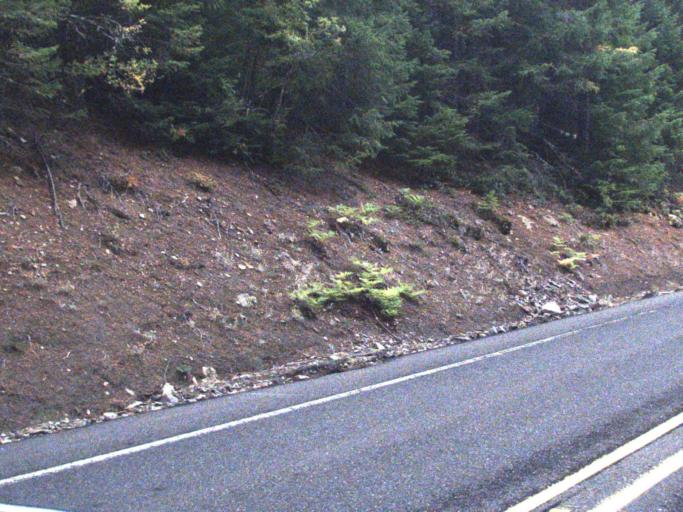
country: US
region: Washington
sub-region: Pierce County
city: Buckley
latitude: 46.6737
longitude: -121.5188
